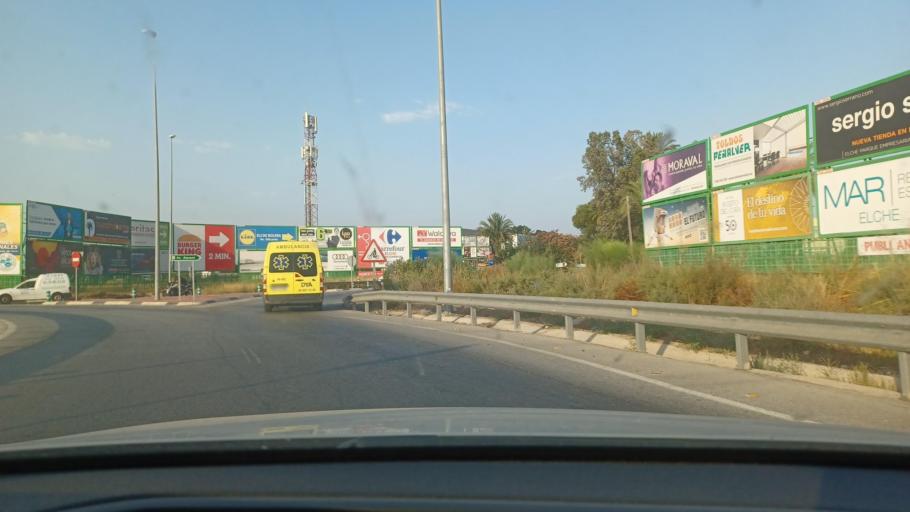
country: ES
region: Valencia
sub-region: Provincia de Alicante
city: Elche
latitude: 38.2751
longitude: -0.6618
